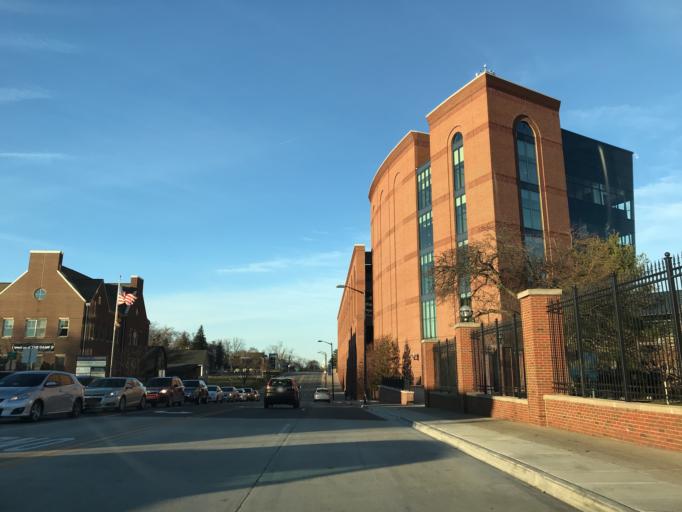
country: US
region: Michigan
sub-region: Washtenaw County
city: Ann Arbor
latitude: 42.2646
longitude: -83.7501
